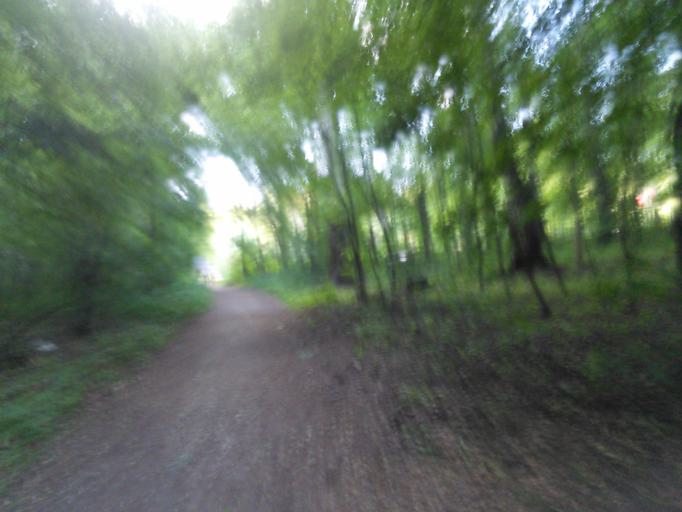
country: RU
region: Moscow
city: Sokol'niki
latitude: 55.8019
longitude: 37.6758
